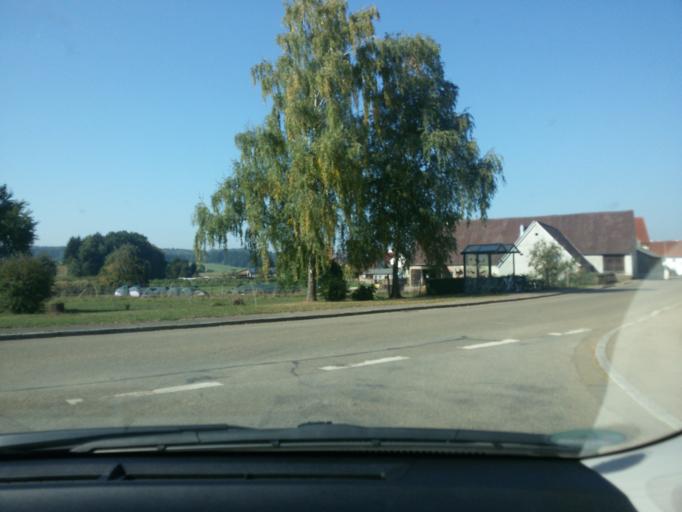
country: DE
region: Bavaria
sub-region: Regierungsbezirk Mittelfranken
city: Wassertrudingen
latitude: 49.0032
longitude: 10.5875
